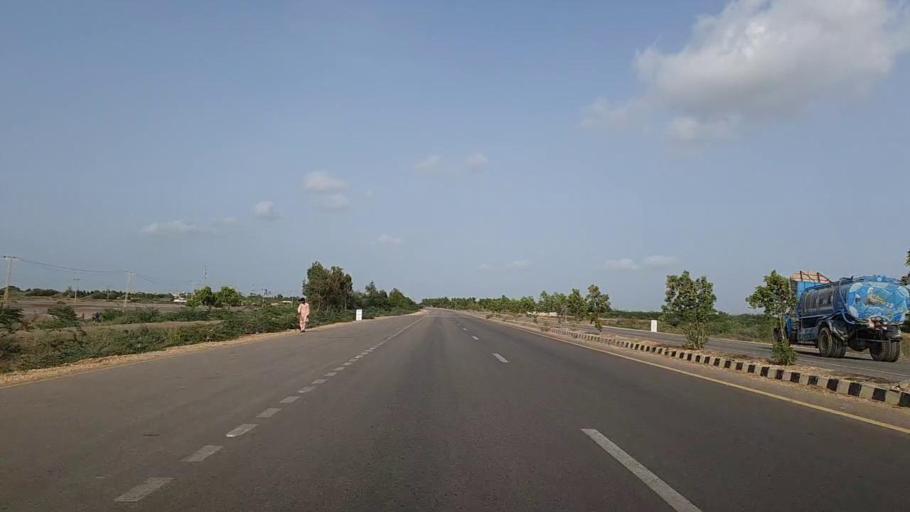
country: PK
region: Sindh
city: Thatta
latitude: 24.7397
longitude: 67.7562
